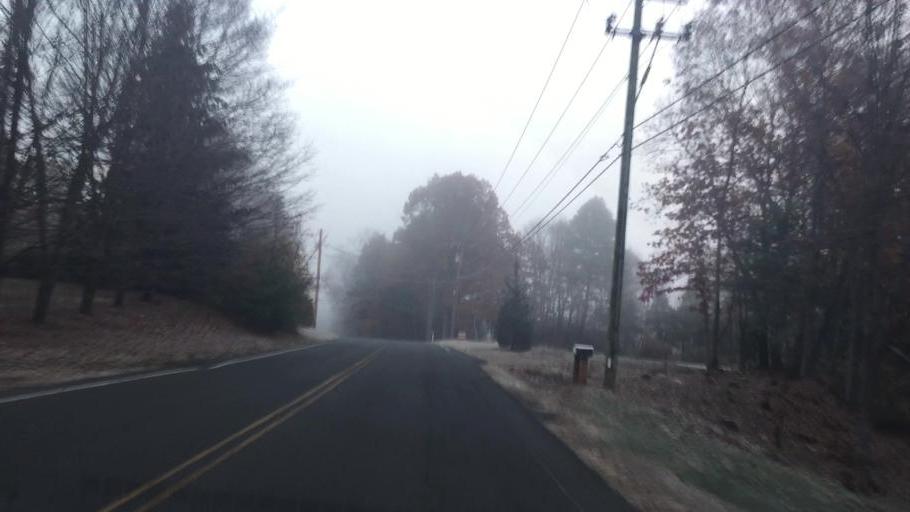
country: US
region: Massachusetts
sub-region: Hampshire County
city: Southampton
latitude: 42.2194
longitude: -72.6898
